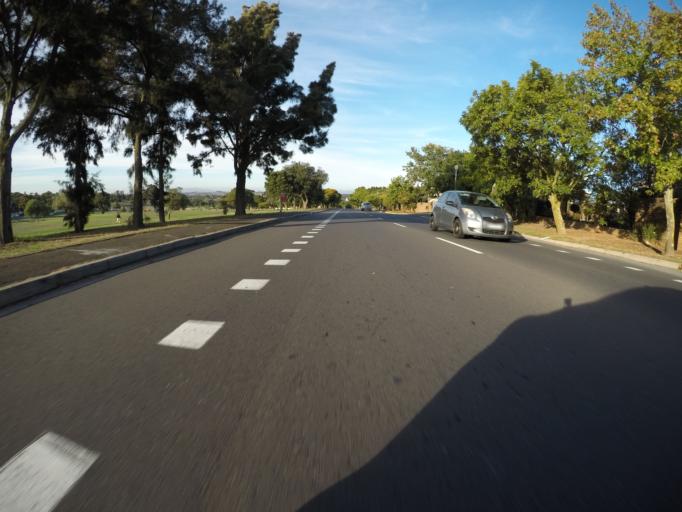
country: ZA
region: Western Cape
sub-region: City of Cape Town
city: Kraaifontein
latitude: -33.8665
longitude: 18.6536
